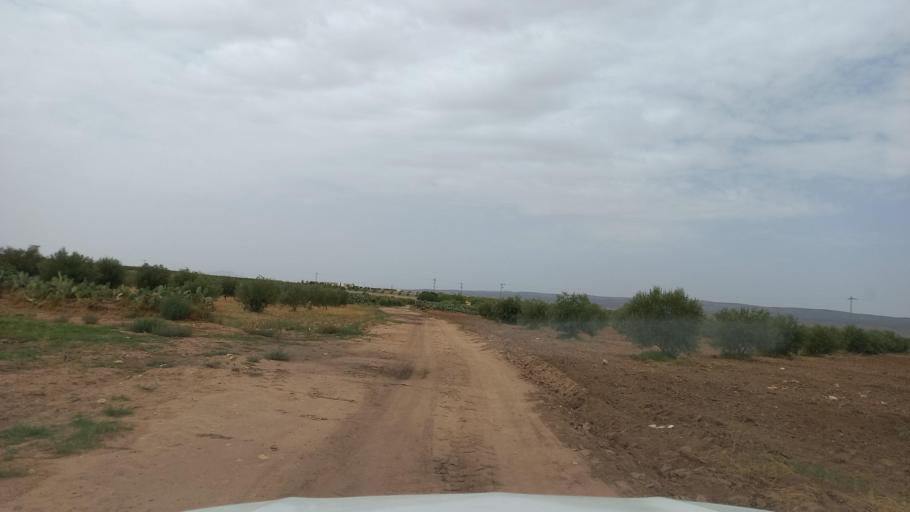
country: TN
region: Al Qasrayn
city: Kasserine
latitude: 35.2867
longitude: 9.0194
